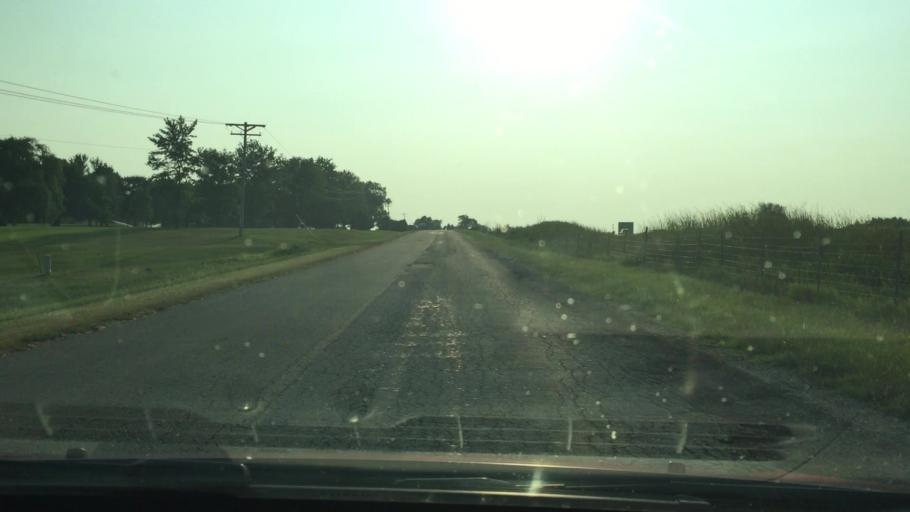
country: US
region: Illinois
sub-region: Bureau County
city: Ladd
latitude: 41.3640
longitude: -89.1927
